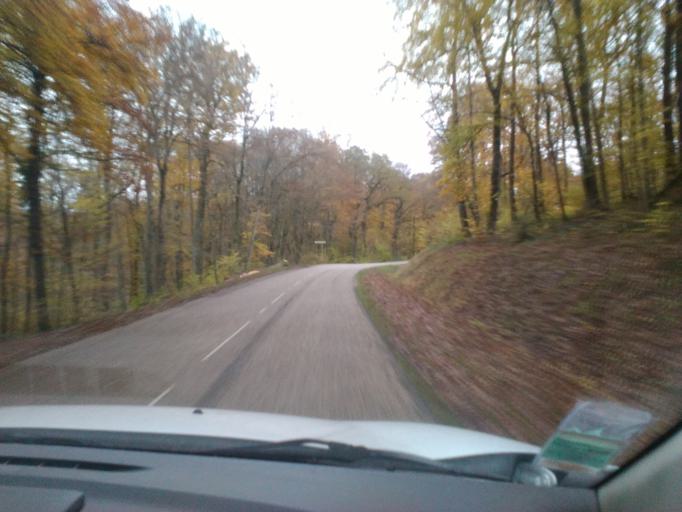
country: FR
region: Lorraine
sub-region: Departement des Vosges
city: Darnieulles
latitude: 48.2375
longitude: 6.2849
